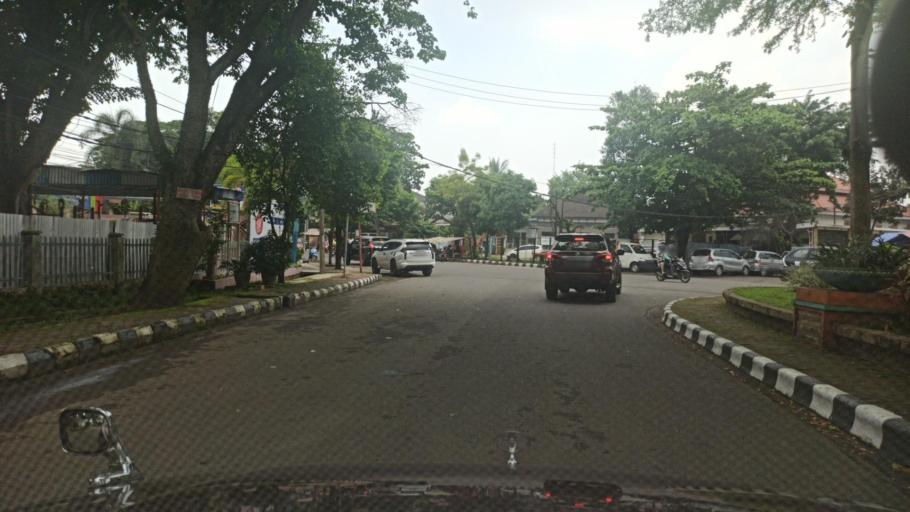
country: ID
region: South Sumatra
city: Plaju
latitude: -2.9920
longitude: 104.7497
